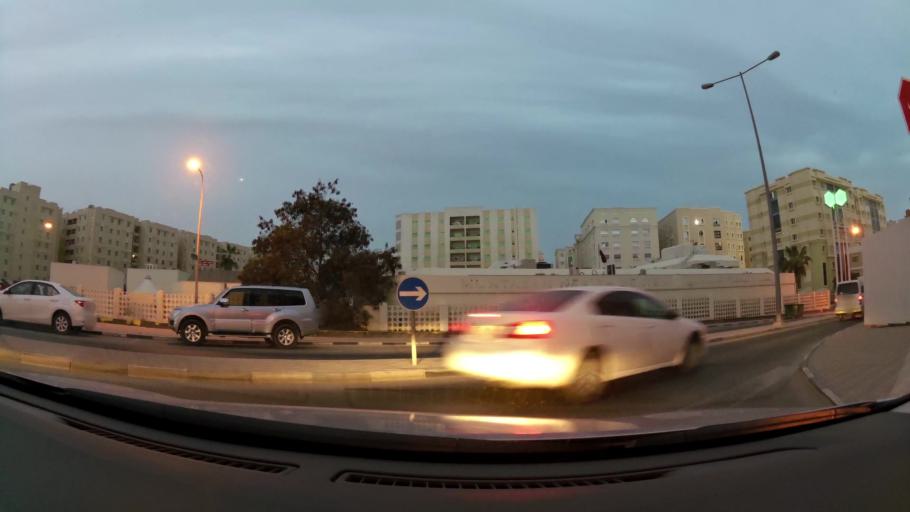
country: QA
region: Baladiyat ad Dawhah
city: Doha
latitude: 25.2721
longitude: 51.5208
